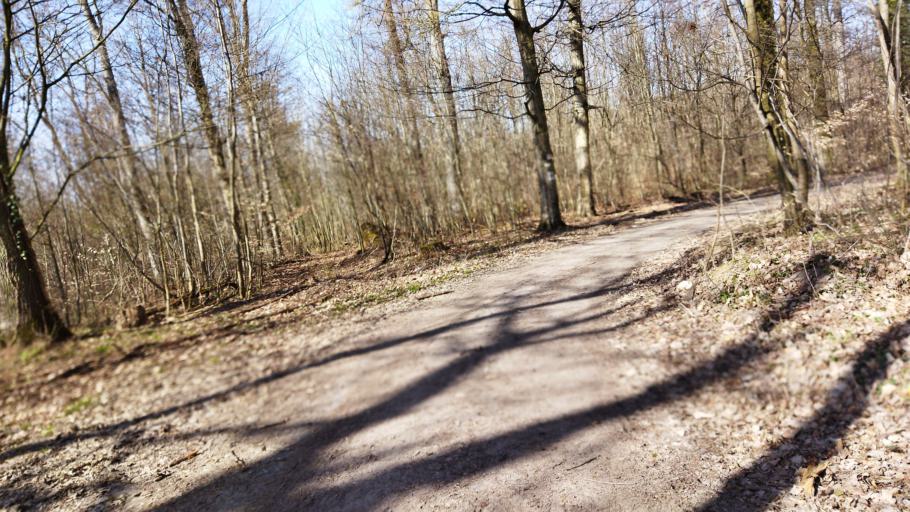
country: DE
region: Baden-Wuerttemberg
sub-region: Regierungsbezirk Stuttgart
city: Eppingen
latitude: 49.1211
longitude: 8.9294
